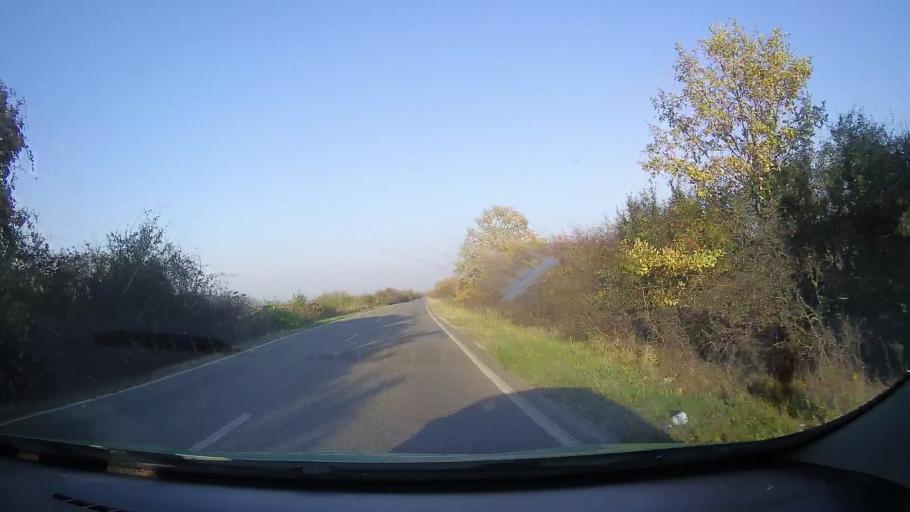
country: RO
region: Arad
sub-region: Comuna Tarnova
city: Chier
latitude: 46.3243
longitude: 21.8314
